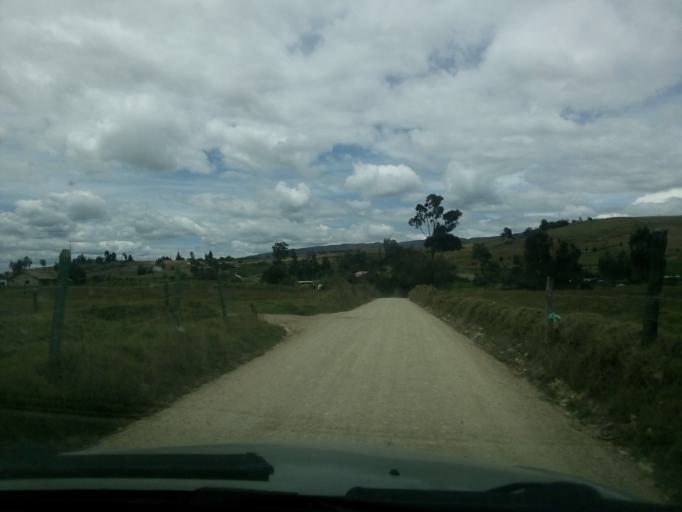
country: CO
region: Boyaca
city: Toca
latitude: 5.5772
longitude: -73.1795
